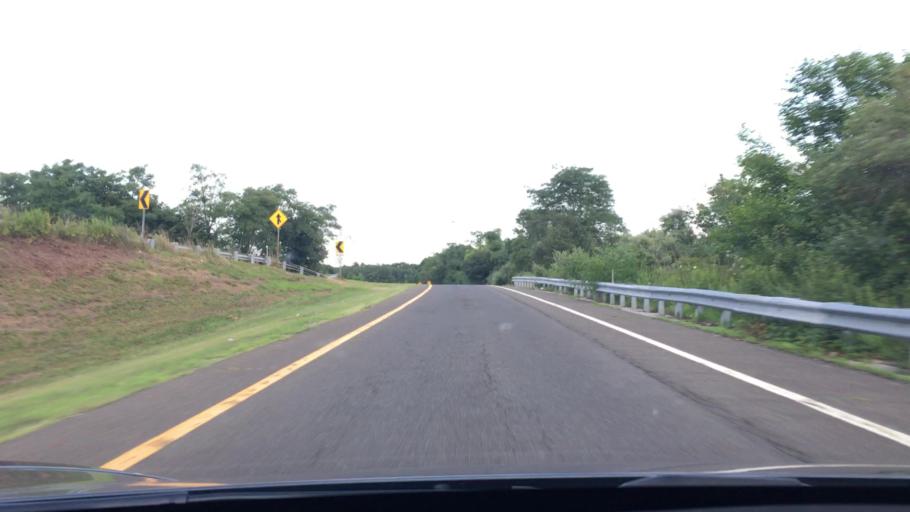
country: US
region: New York
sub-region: Suffolk County
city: Commack
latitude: 40.8038
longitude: -73.2838
